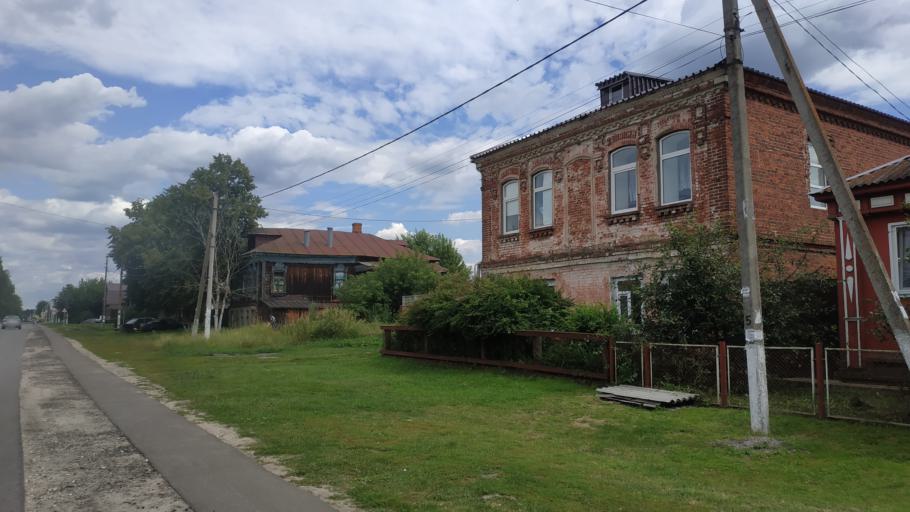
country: RU
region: Moskovskaya
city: Beloomut
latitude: 54.9392
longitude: 39.3426
